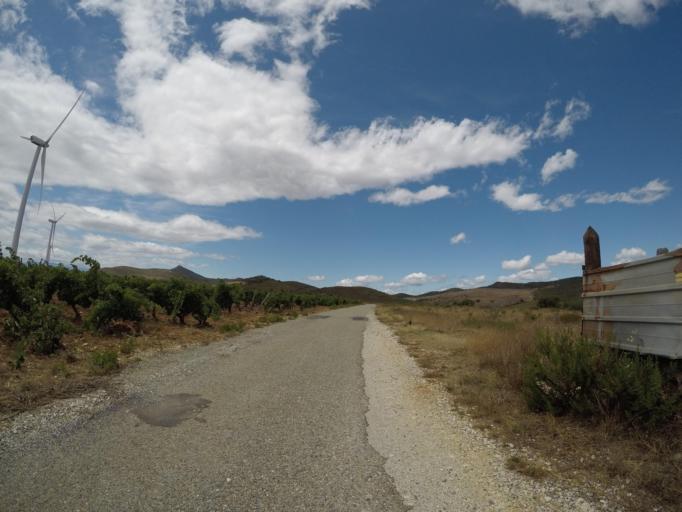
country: FR
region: Languedoc-Roussillon
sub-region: Departement des Pyrenees-Orientales
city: Corneilla-la-Riviere
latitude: 42.7243
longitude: 2.7493
